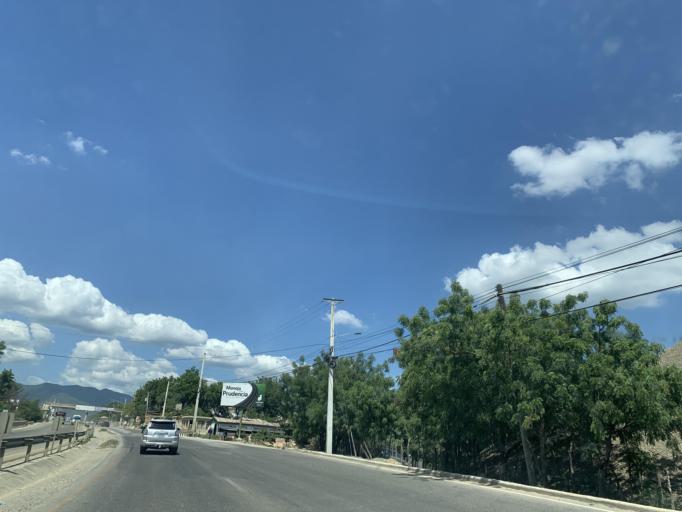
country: DO
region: Santiago
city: Villa Bisono
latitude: 19.5479
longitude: -70.8492
